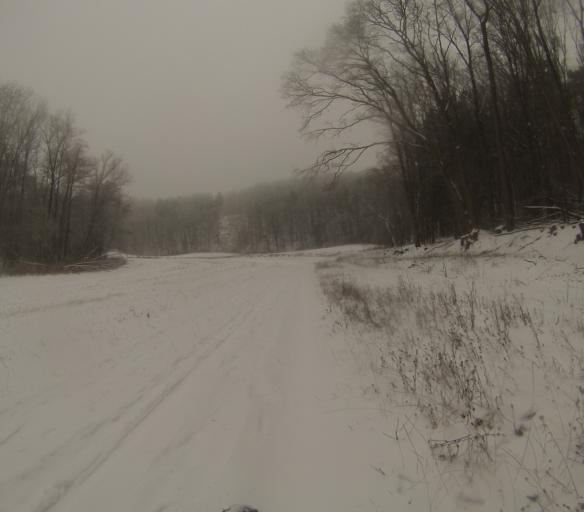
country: CZ
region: South Moravian
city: Strelice
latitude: 49.1353
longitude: 16.5003
